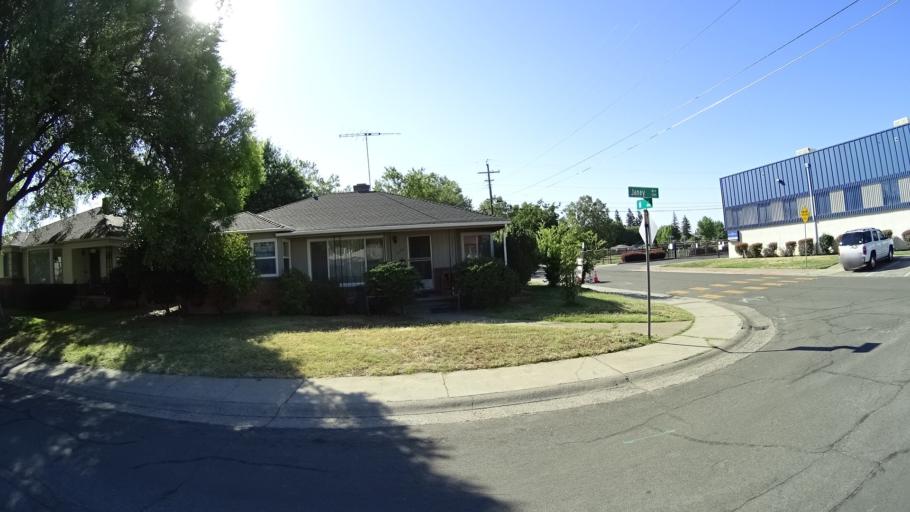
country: US
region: California
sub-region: Sacramento County
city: Sacramento
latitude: 38.5598
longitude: -121.4336
